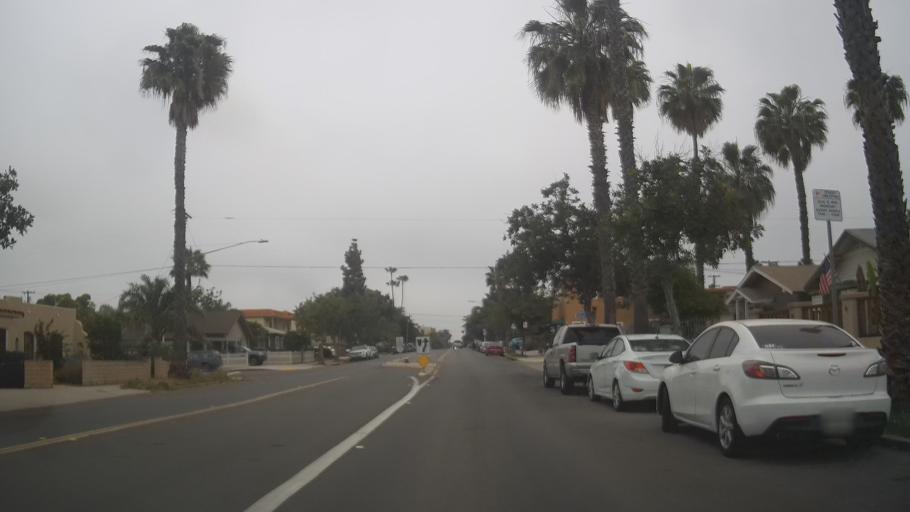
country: US
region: California
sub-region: San Diego County
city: San Diego
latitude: 32.7499
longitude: -117.1388
